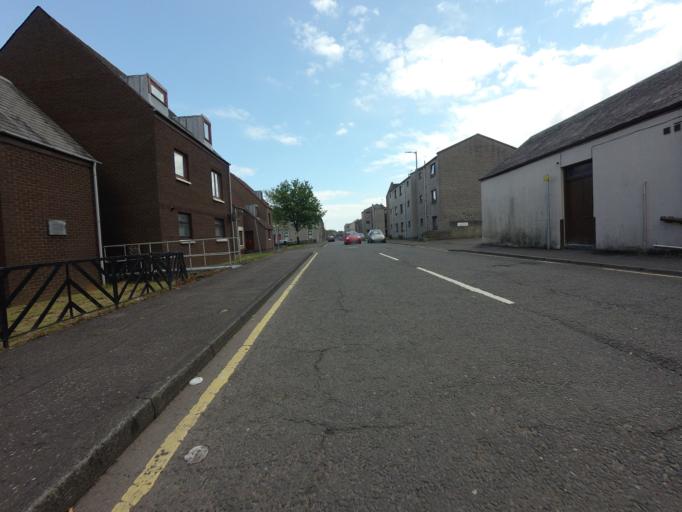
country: GB
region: Scotland
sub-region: Falkirk
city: Falkirk
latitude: 56.0061
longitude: -3.7840
